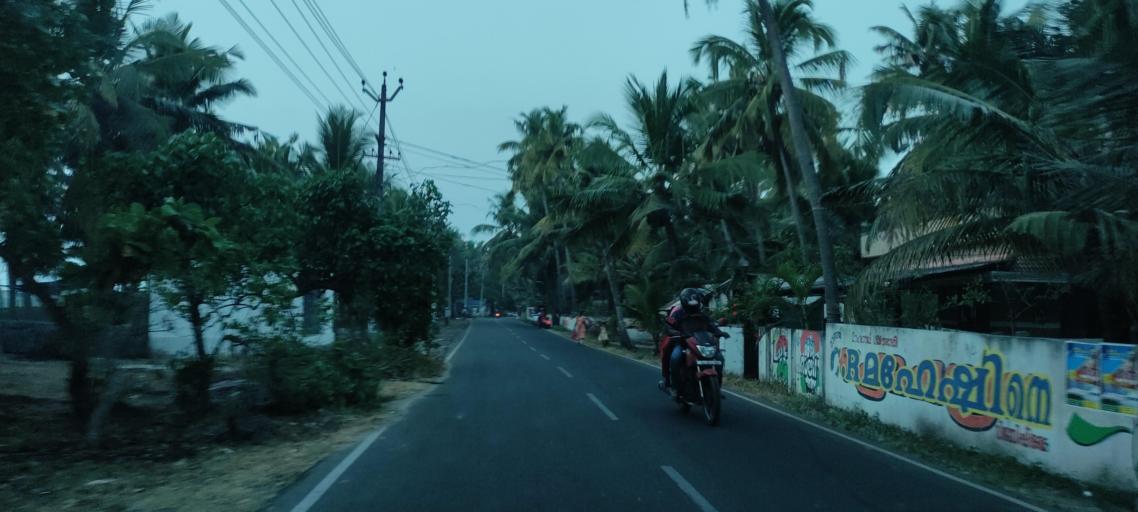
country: IN
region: Kerala
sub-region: Alappuzha
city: Kayankulam
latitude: 9.1188
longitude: 76.4713
